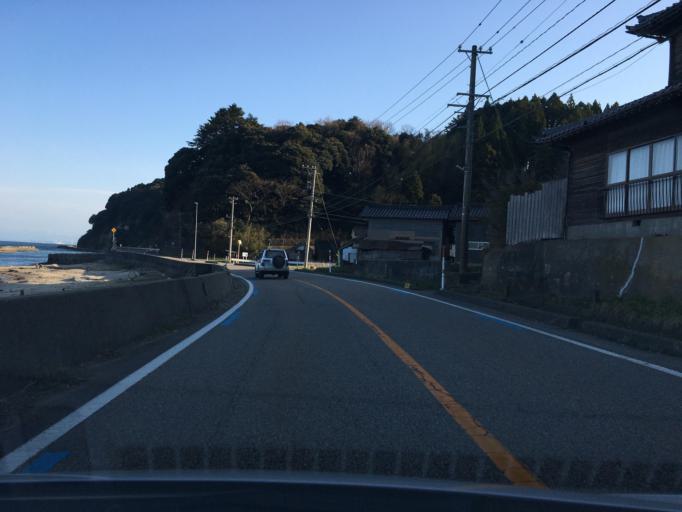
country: JP
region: Toyama
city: Himi
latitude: 36.9362
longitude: 137.0269
